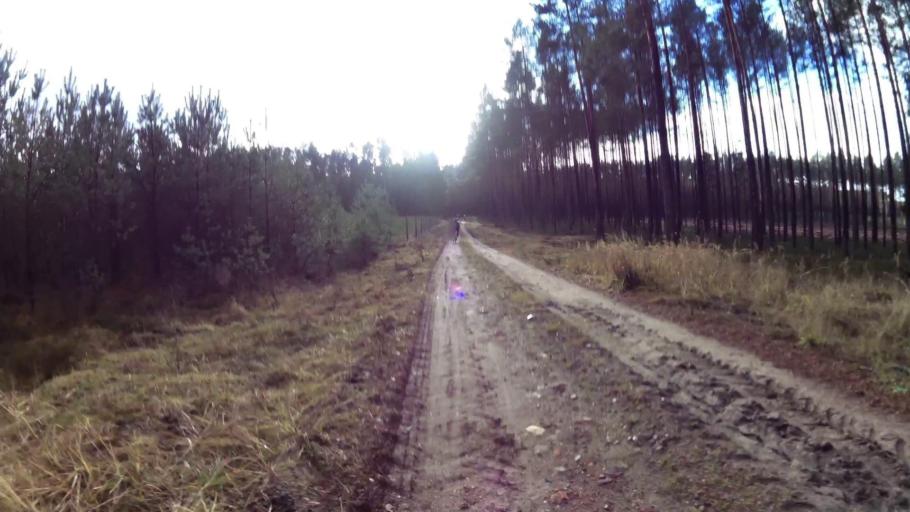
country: PL
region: West Pomeranian Voivodeship
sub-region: Powiat koszalinski
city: Sianow
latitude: 54.0855
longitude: 16.2917
